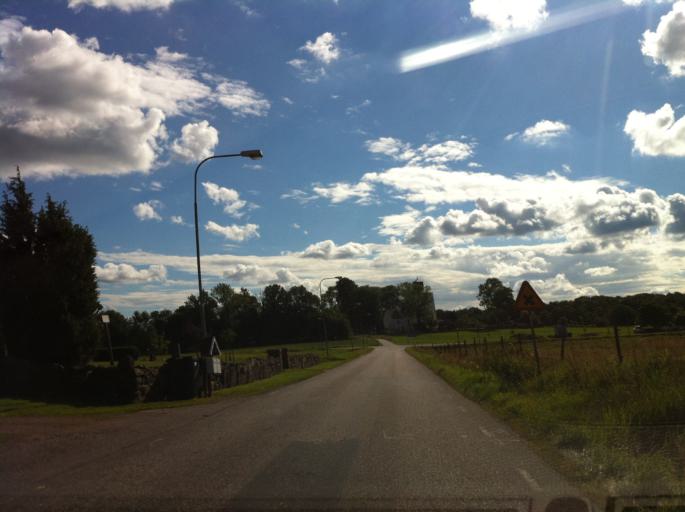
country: SE
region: Skane
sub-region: Hassleholms Kommun
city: Sosdala
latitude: 56.0285
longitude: 13.5884
